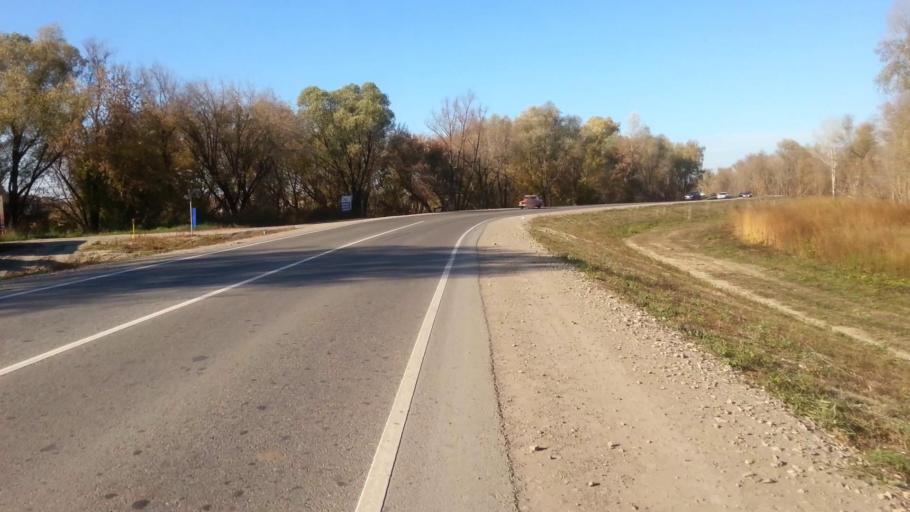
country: RU
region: Altai Krai
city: Sannikovo
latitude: 53.3215
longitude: 83.9430
